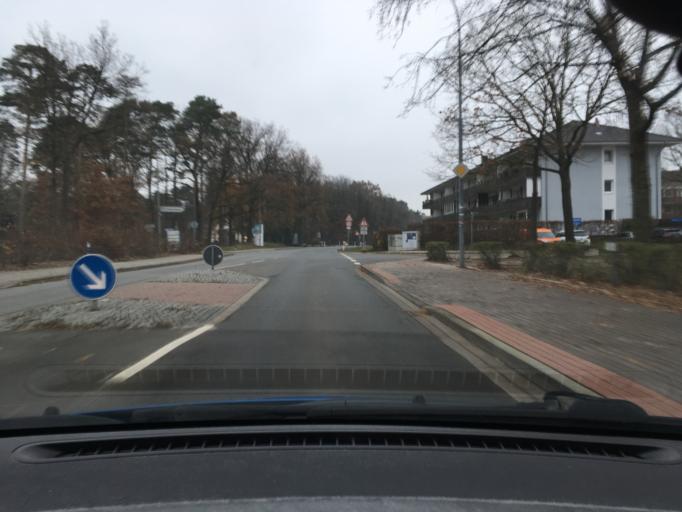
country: DE
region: Lower Saxony
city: Soltau
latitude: 52.9939
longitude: 9.8499
